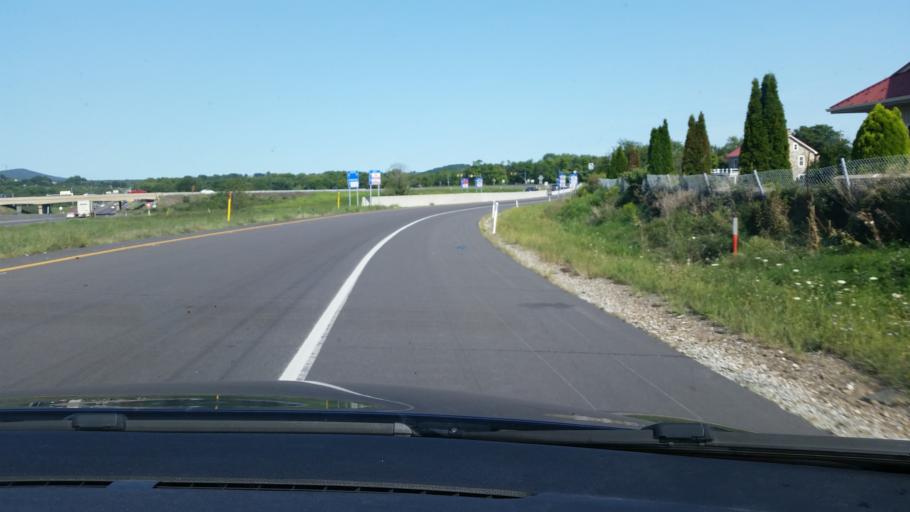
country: US
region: Pennsylvania
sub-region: Berks County
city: West Hamburg
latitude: 40.5557
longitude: -76.0011
